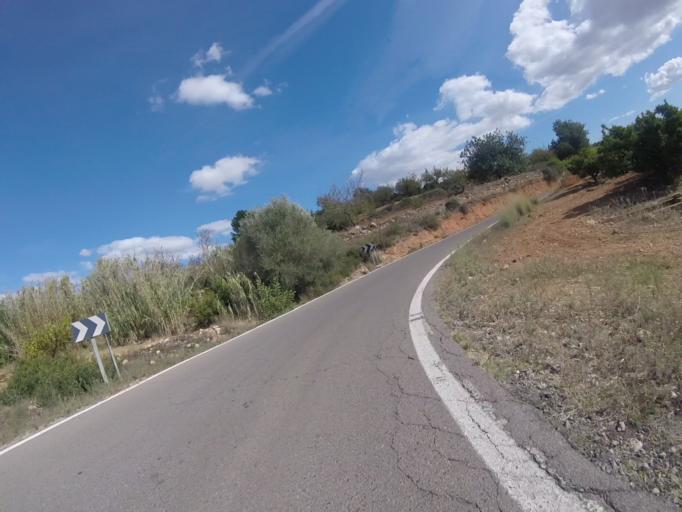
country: ES
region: Valencia
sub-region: Provincia de Castello
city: Cuevas de Vinroma
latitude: 40.3713
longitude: 0.1169
